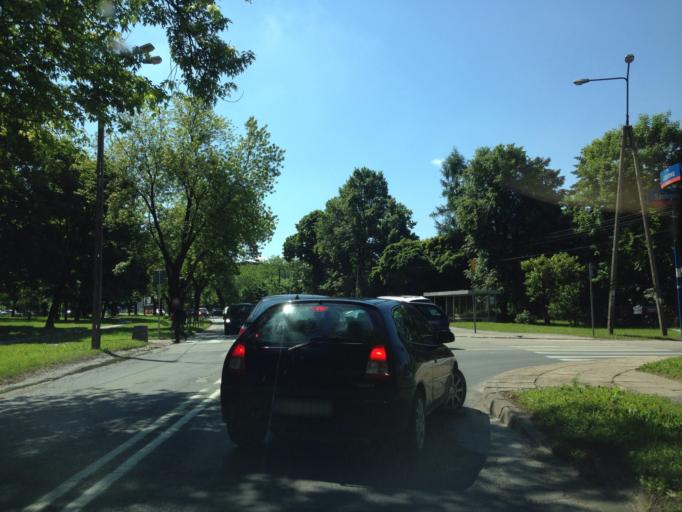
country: PL
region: Masovian Voivodeship
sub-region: Warszawa
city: Ursus
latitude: 52.2202
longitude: 20.8975
